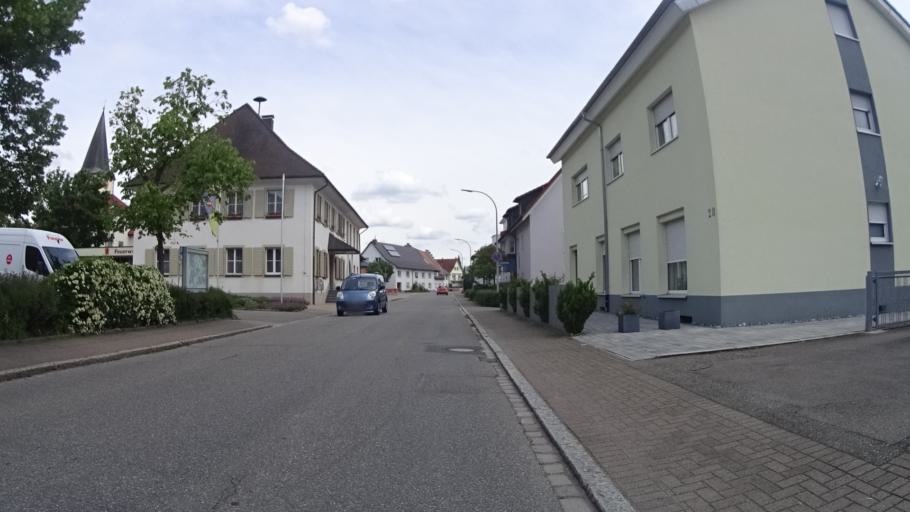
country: CH
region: Aargau
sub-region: Bezirk Rheinfelden
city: Kaiseraugst
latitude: 47.5567
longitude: 7.7328
